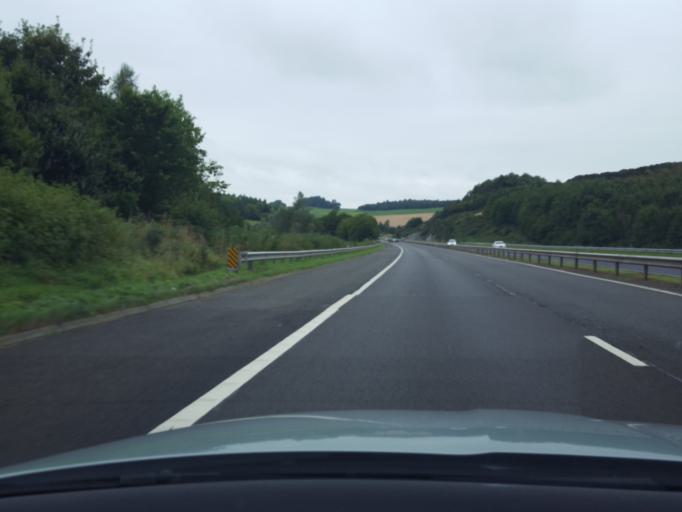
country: GB
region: Scotland
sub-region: Perth and Kinross
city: Milnathort
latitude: 56.2625
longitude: -3.3793
